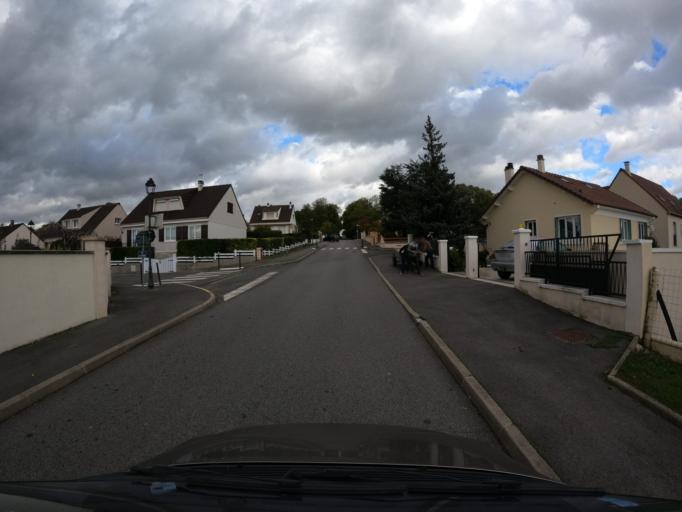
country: FR
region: Ile-de-France
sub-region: Departement de Seine-et-Marne
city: Coupvray
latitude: 48.8986
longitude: 2.7923
